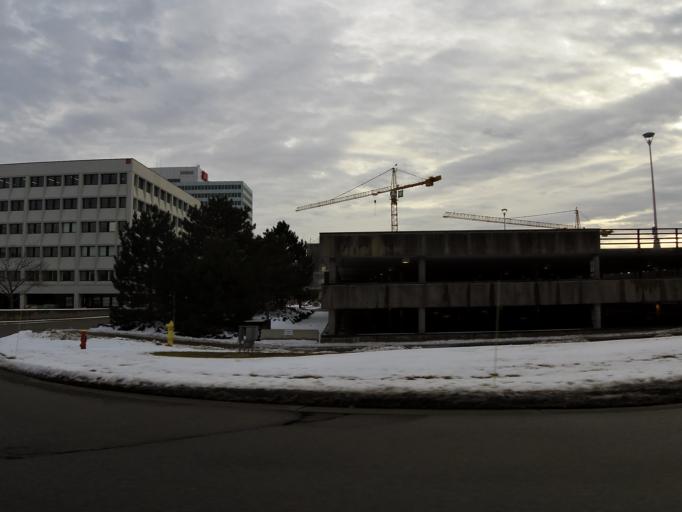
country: US
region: Minnesota
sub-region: Ramsey County
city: Maplewood
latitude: 44.9532
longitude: -92.9972
